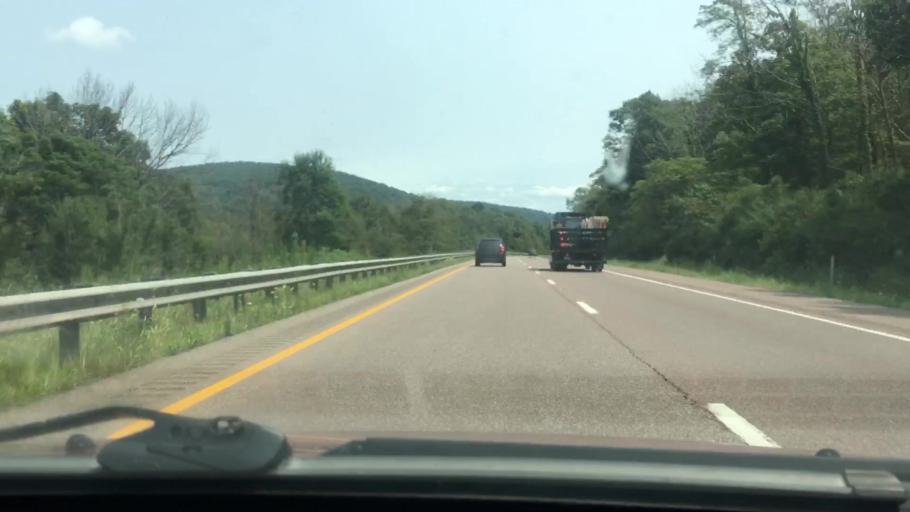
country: US
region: Maryland
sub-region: Allegany County
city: Frostburg
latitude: 39.6407
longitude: -78.8860
